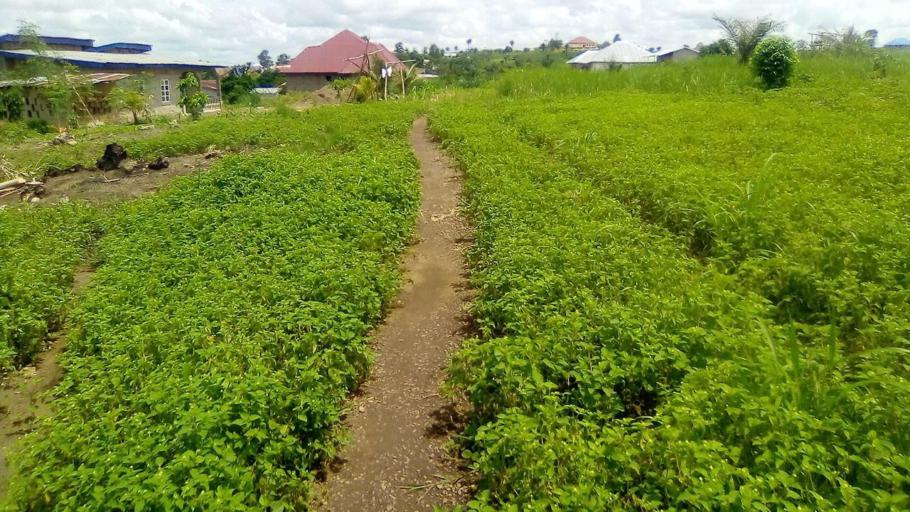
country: SL
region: Southern Province
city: Bo
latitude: 7.9355
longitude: -11.7468
